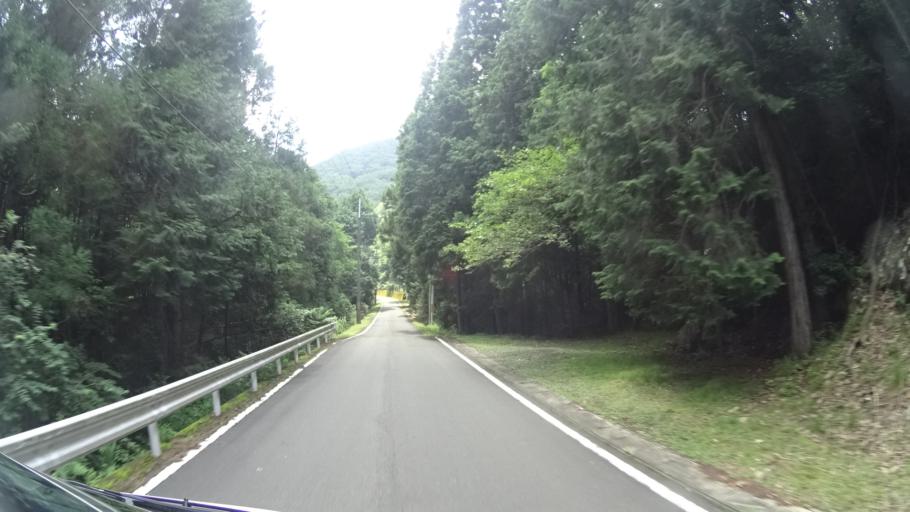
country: JP
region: Hyogo
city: Sasayama
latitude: 35.1854
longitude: 135.2166
